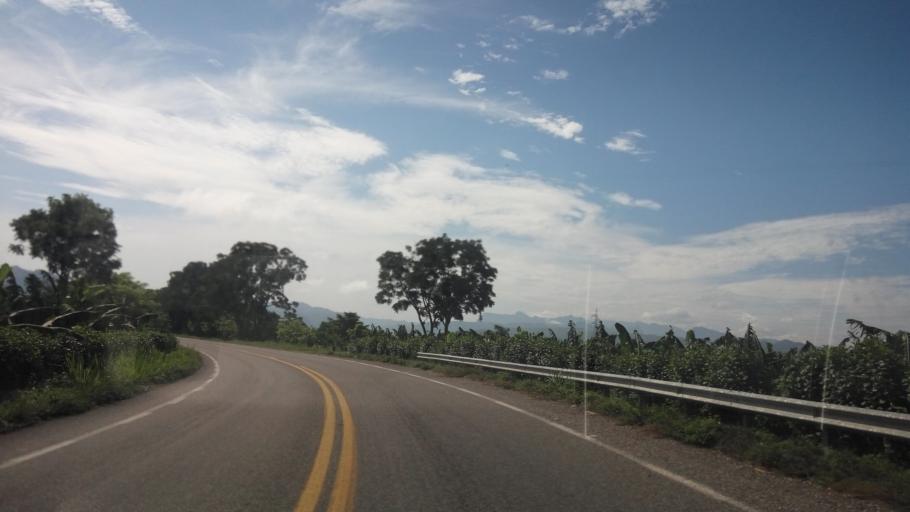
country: MX
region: Tabasco
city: Teapa
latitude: 17.6043
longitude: -92.9667
